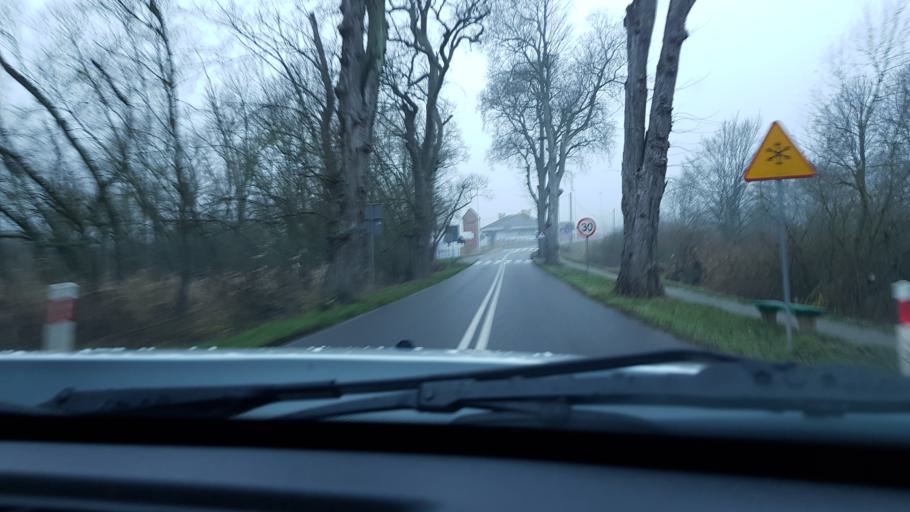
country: DE
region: Brandenburg
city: Mescherin
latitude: 53.2543
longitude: 14.4457
